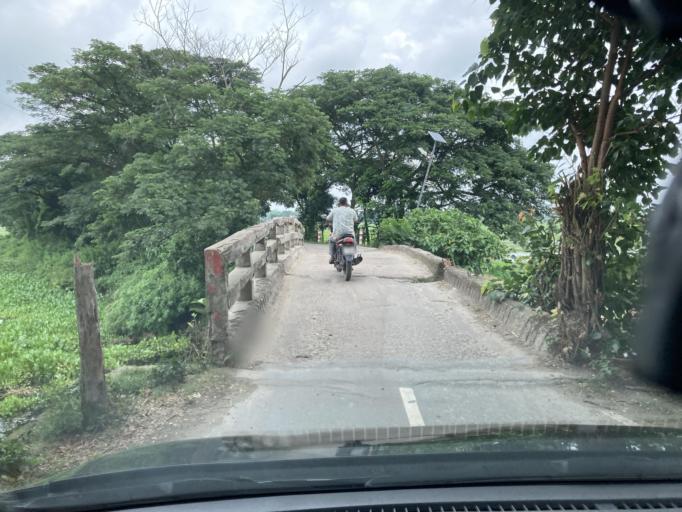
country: BD
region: Dhaka
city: Azimpur
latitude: 23.7751
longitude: 90.2069
